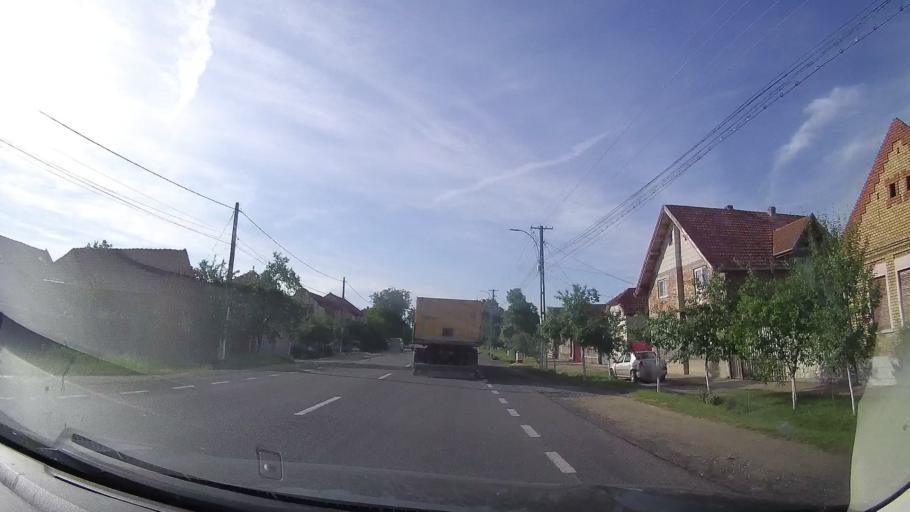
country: RO
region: Timis
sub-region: Comuna Costeiu
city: Costeiu
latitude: 45.7309
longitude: 21.8676
